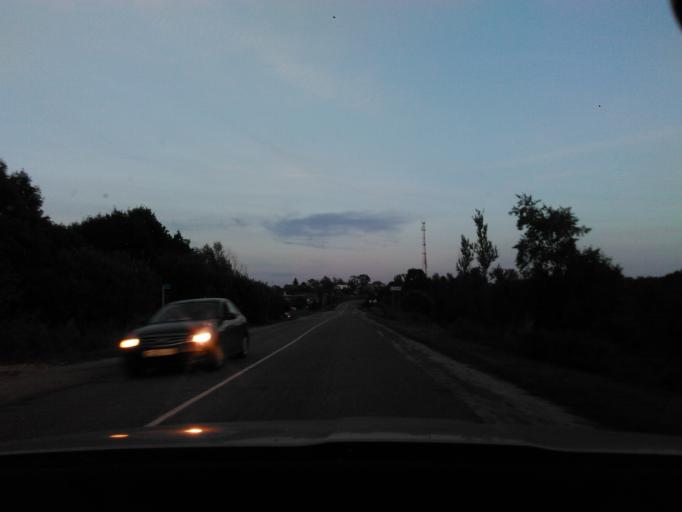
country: RU
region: Moskovskaya
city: Klin
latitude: 56.2540
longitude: 36.7582
